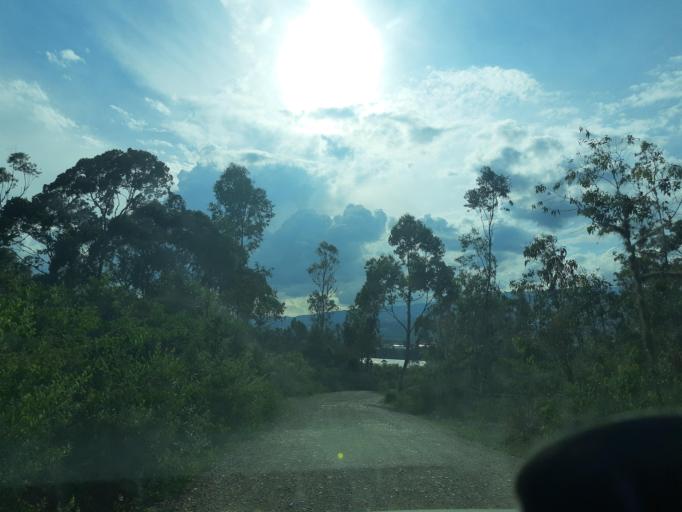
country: CO
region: Boyaca
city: Villa de Leiva
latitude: 5.6637
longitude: -73.5702
